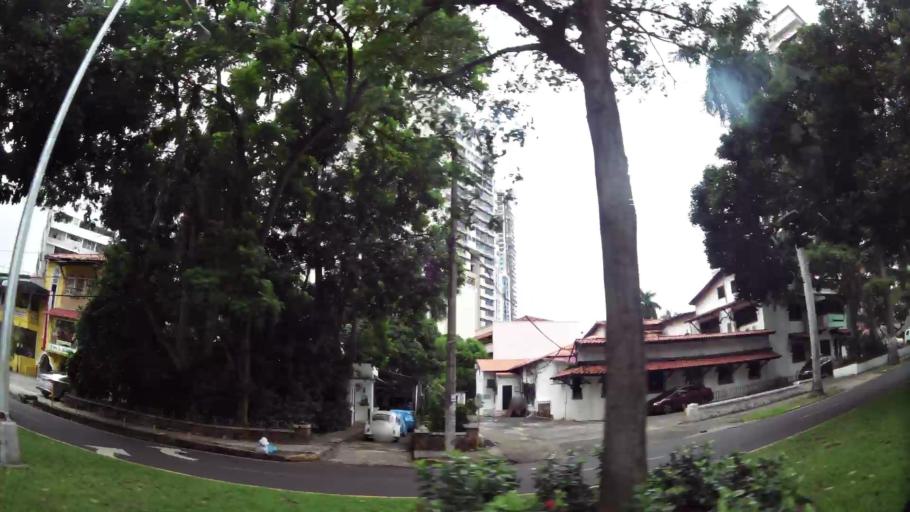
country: PA
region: Panama
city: Panama
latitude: 8.9766
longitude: -79.5269
